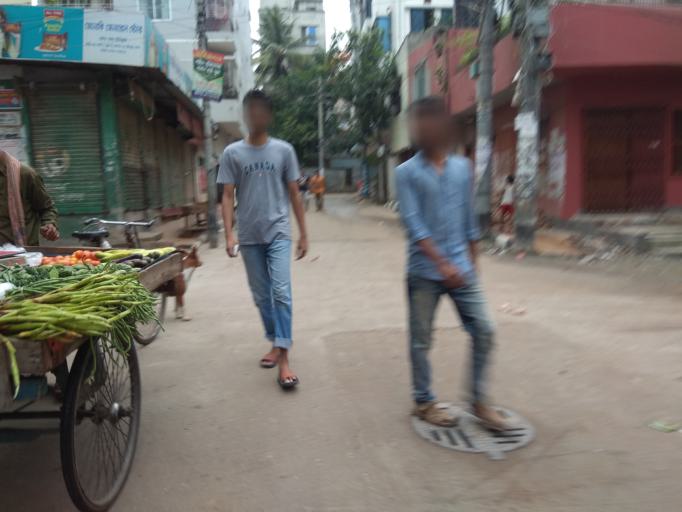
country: BD
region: Dhaka
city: Tungi
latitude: 23.8247
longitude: 90.3742
